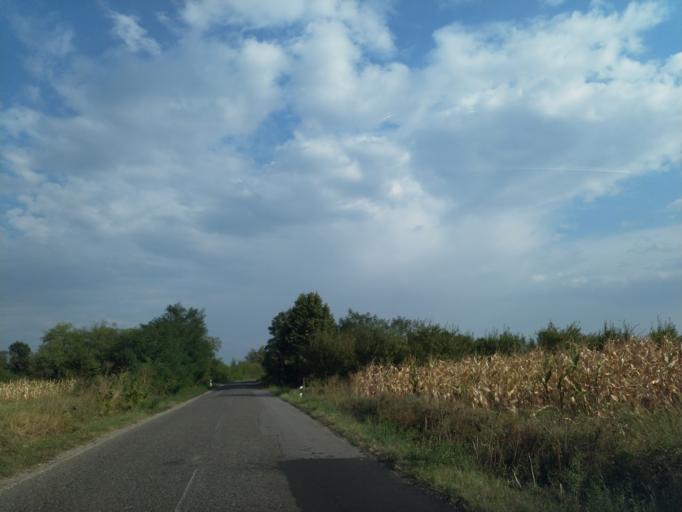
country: RS
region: Central Serbia
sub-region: Pomoravski Okrug
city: Paracin
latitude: 43.8461
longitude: 21.4676
